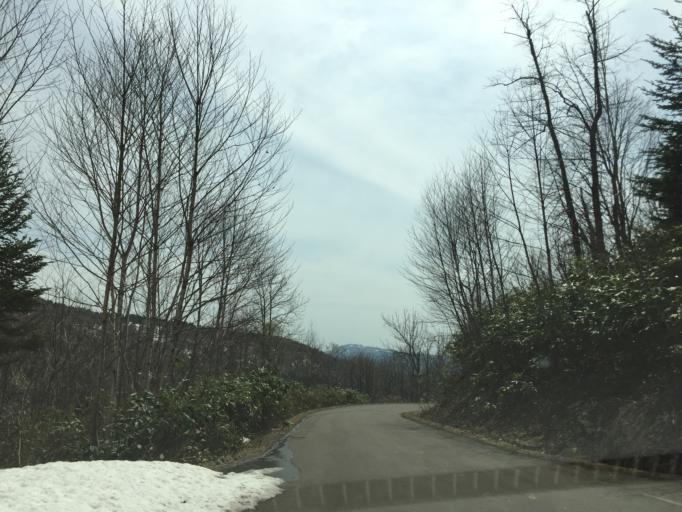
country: JP
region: Hokkaido
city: Akabira
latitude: 43.6002
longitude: 142.0651
